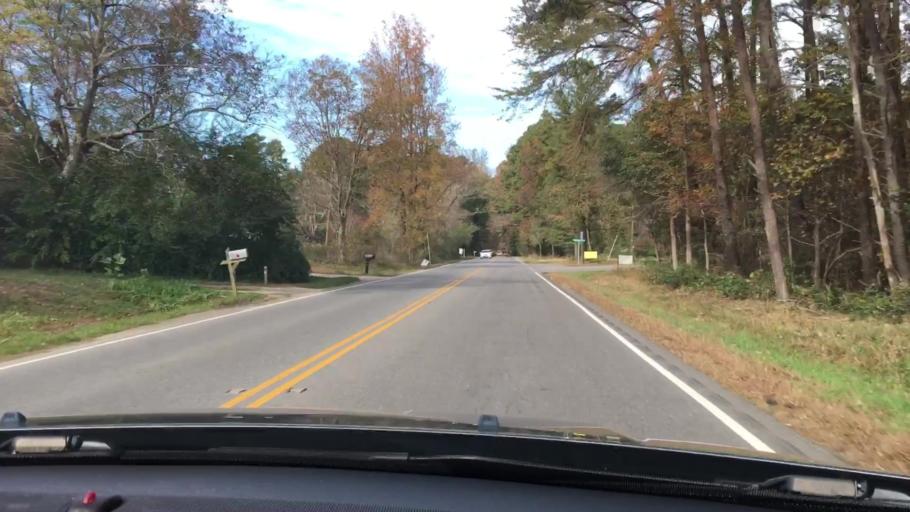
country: US
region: Virginia
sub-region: King William County
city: West Point
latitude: 37.4380
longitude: -76.8362
